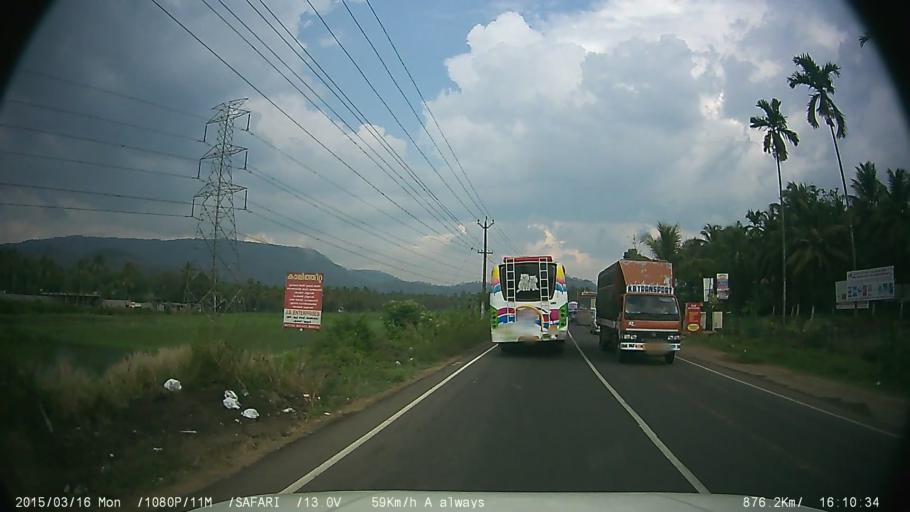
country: IN
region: Kerala
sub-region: Thrissur District
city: Trichur
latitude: 10.5525
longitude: 76.3105
